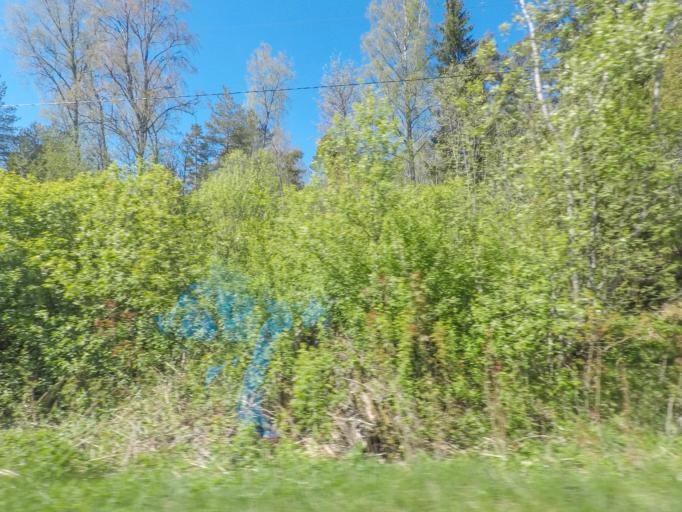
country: FI
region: Uusimaa
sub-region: Helsinki
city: Sammatti
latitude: 60.3644
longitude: 23.8055
